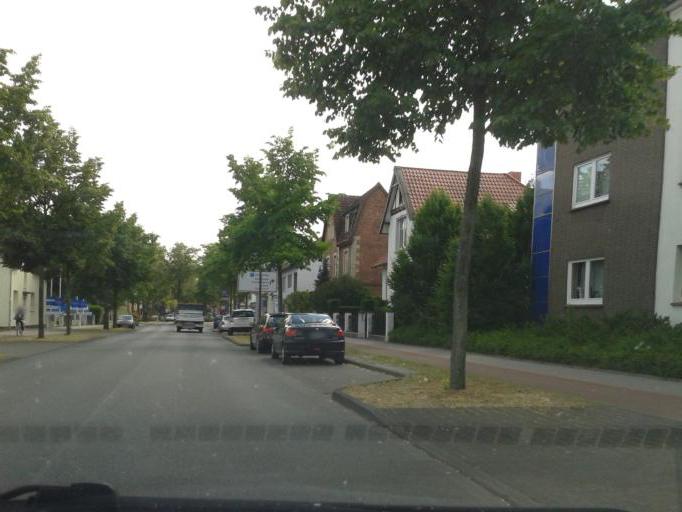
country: DE
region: North Rhine-Westphalia
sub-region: Regierungsbezirk Detmold
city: Paderborn
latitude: 51.7503
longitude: 8.7159
